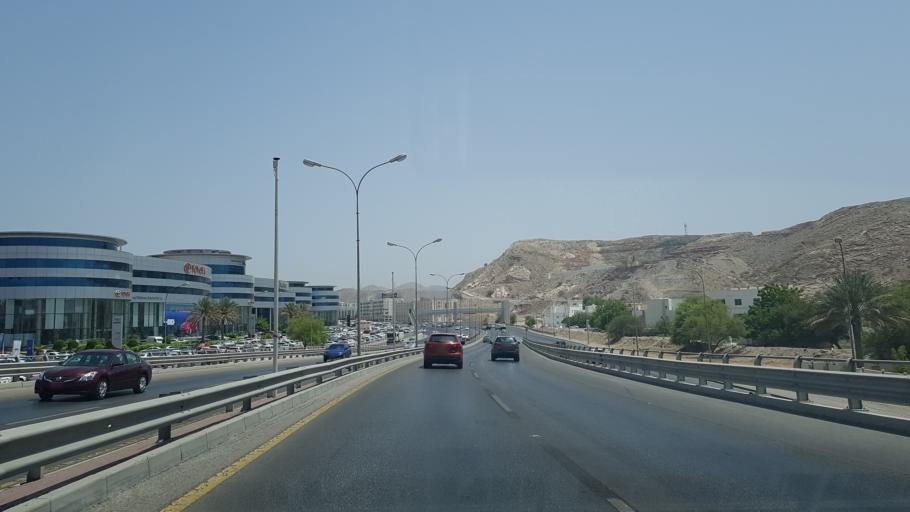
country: OM
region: Muhafazat Masqat
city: Muscat
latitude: 23.6052
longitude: 58.5122
